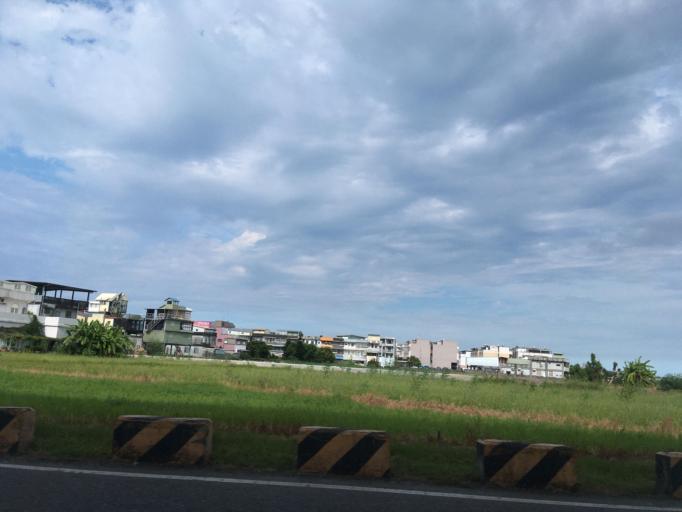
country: TW
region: Taiwan
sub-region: Yilan
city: Yilan
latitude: 24.6831
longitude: 121.7927
